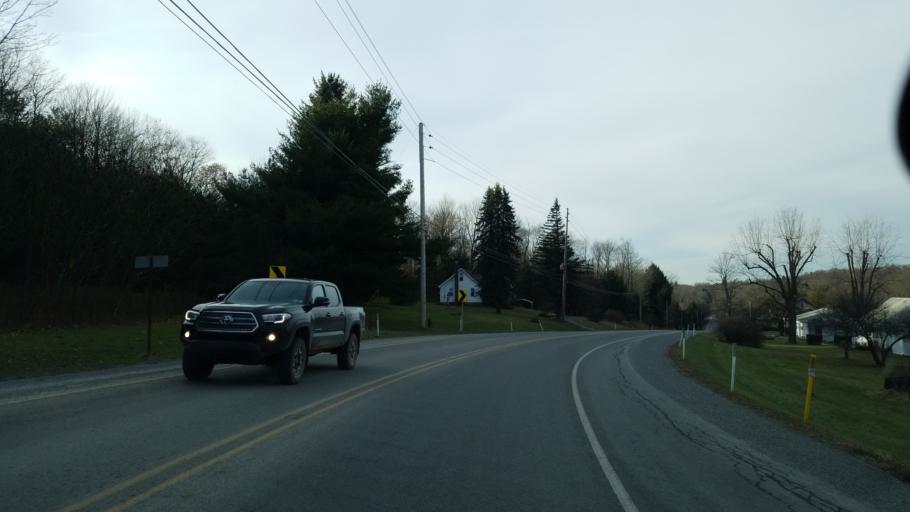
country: US
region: Pennsylvania
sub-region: Clearfield County
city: DuBois
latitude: 41.0242
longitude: -78.6655
